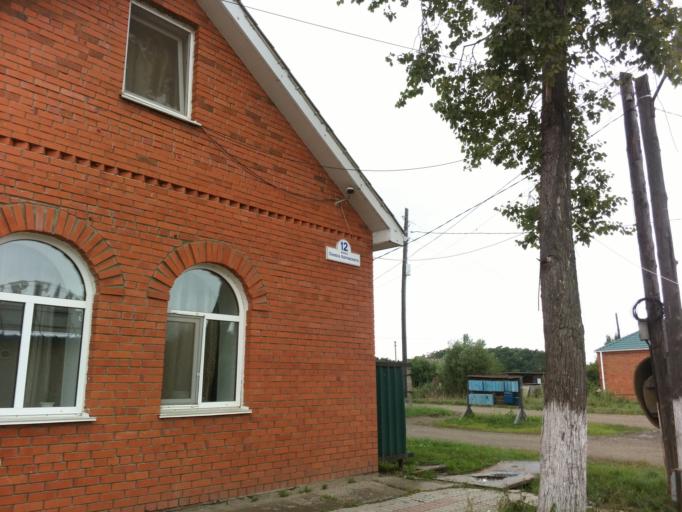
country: RU
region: Primorskiy
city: Dal'nerechensk
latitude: 45.8803
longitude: 133.7278
